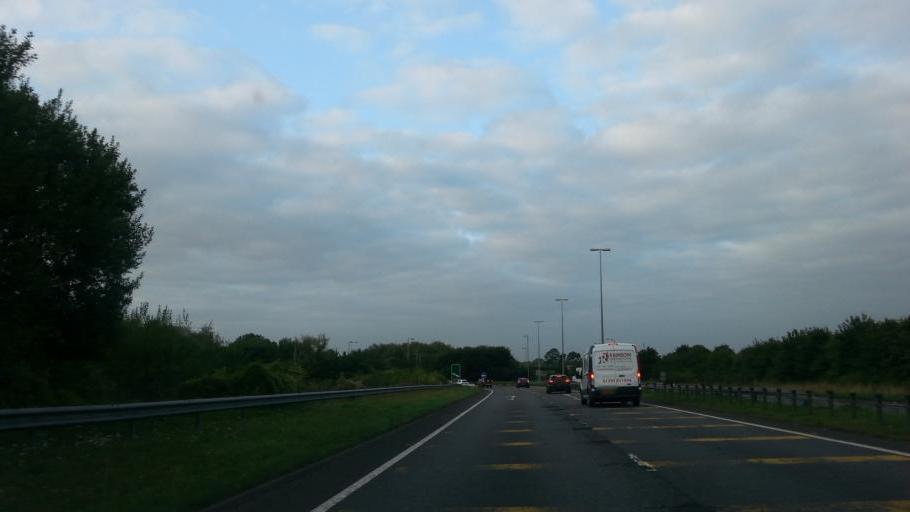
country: GB
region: England
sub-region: Northamptonshire
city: Brackley
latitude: 51.9949
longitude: -1.1622
